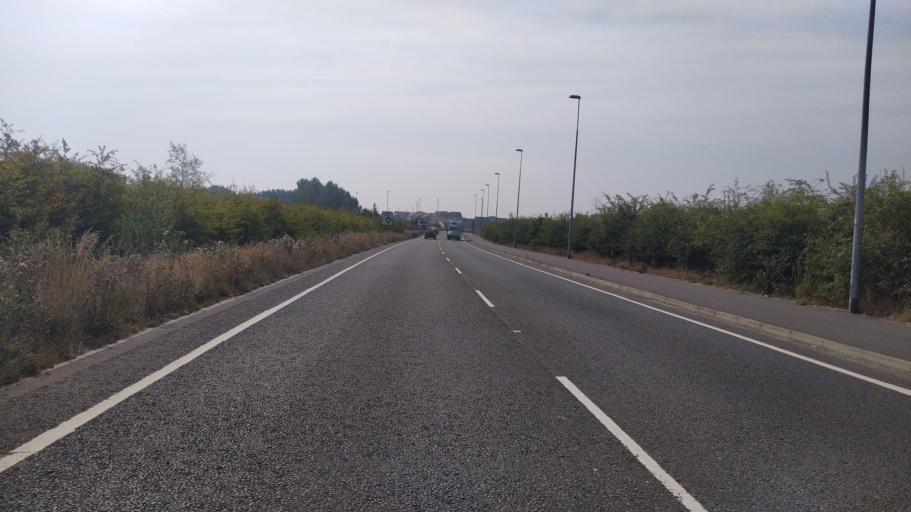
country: GB
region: England
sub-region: West Sussex
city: Barnham
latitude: 50.8045
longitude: -0.6467
